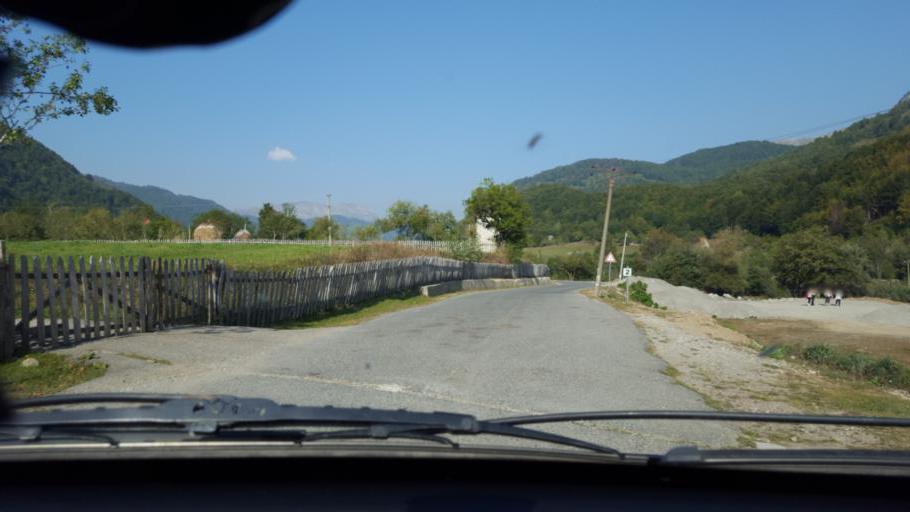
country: ME
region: Andrijevica
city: Andrijevica
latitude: 42.5875
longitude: 19.7152
